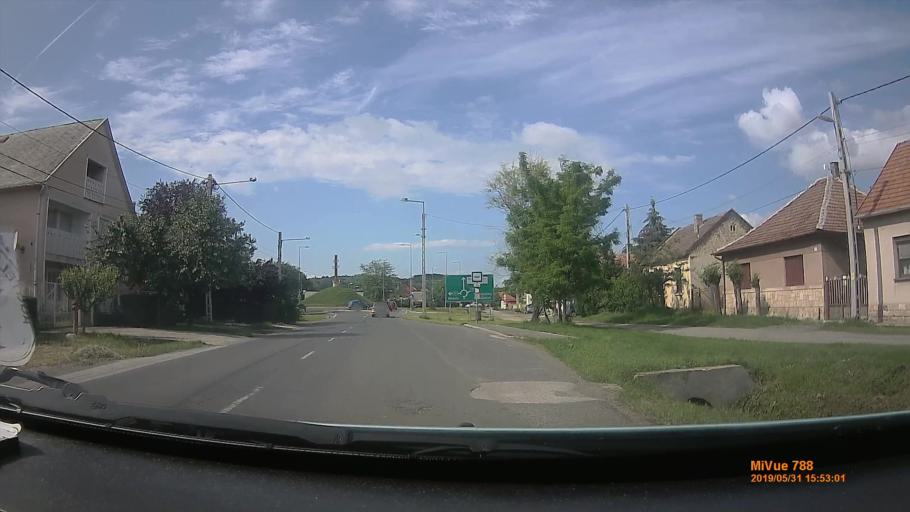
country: HU
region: Borsod-Abauj-Zemplen
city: Szerencs
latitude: 48.1553
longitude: 21.2015
